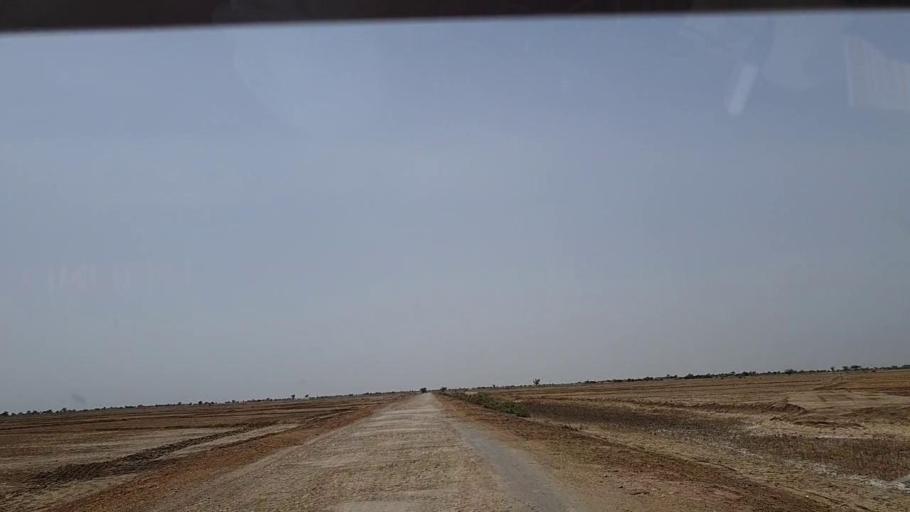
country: PK
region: Sindh
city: Johi
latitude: 26.7372
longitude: 67.6337
